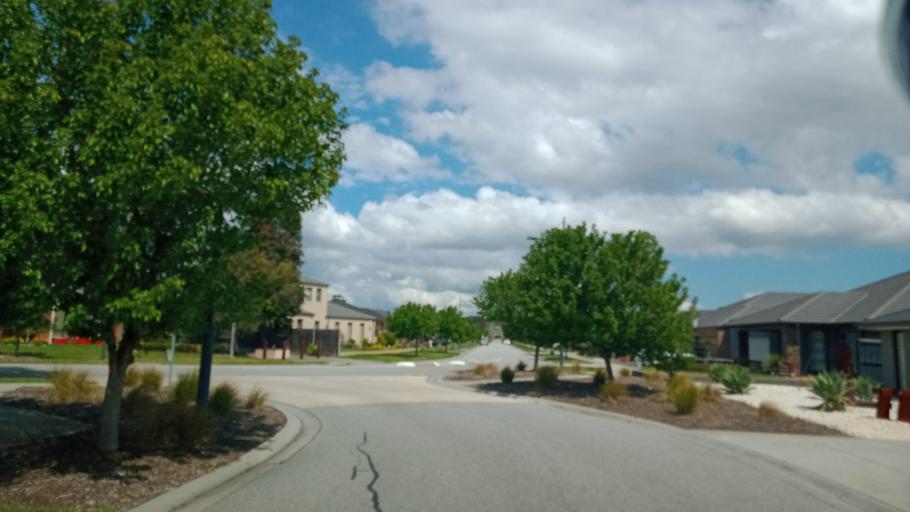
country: AU
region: Victoria
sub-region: Frankston
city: Sandhurst
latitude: -38.0843
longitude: 145.1936
